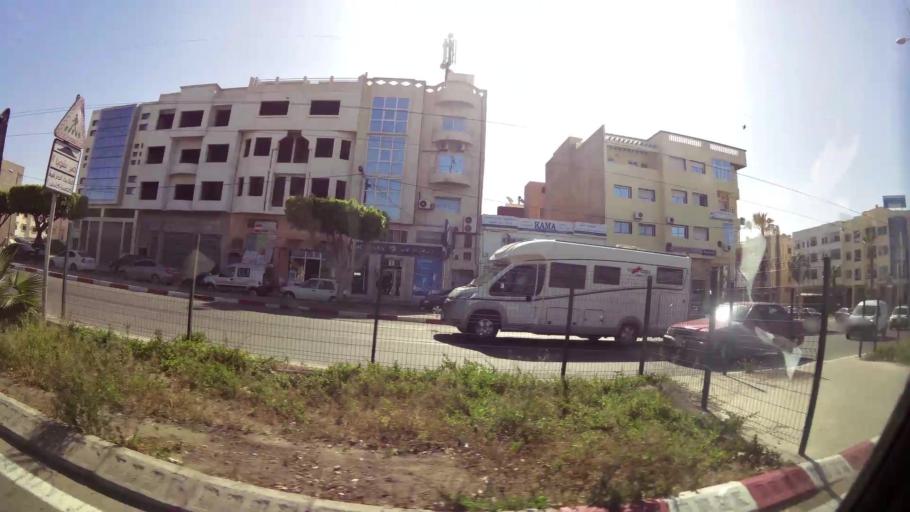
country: MA
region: Souss-Massa-Draa
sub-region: Inezgane-Ait Mellou
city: Inezgane
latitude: 30.3813
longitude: -9.5048
